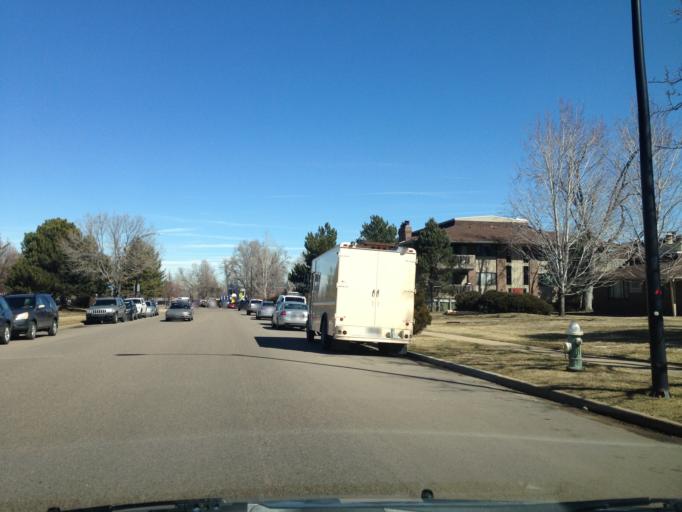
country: US
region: Colorado
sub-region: Boulder County
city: Boulder
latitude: 39.9977
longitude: -105.2293
